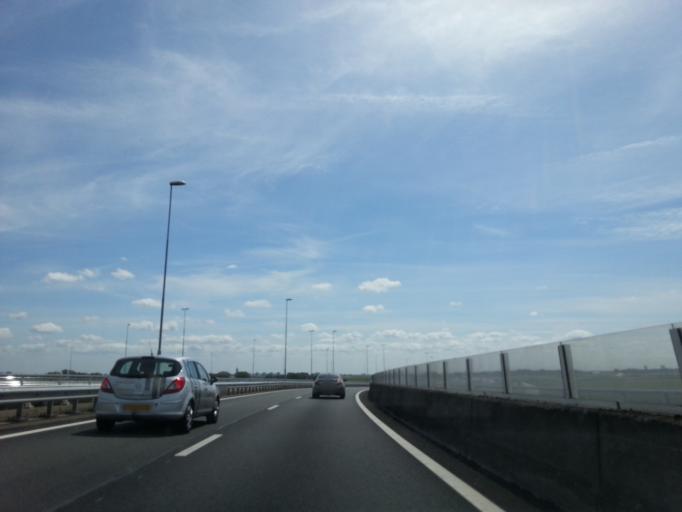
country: NL
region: North Holland
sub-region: Gemeente Haarlemmermeer
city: Hoofddorp
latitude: 52.3546
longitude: 4.7369
